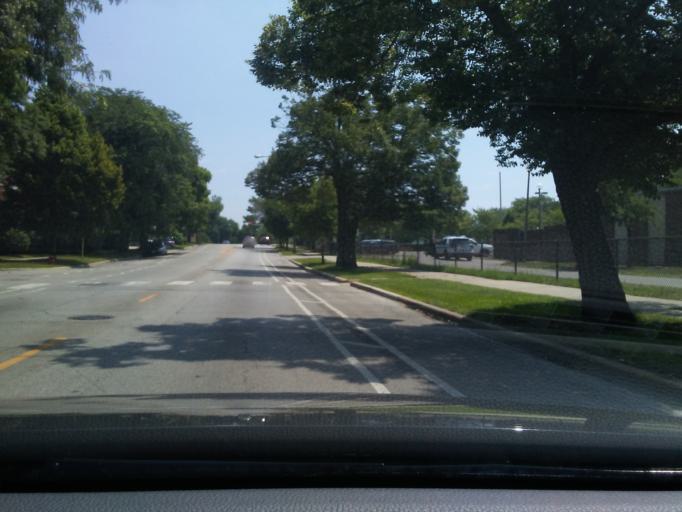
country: US
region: Illinois
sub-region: Cook County
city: Evanston
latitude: 42.0052
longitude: -87.6820
